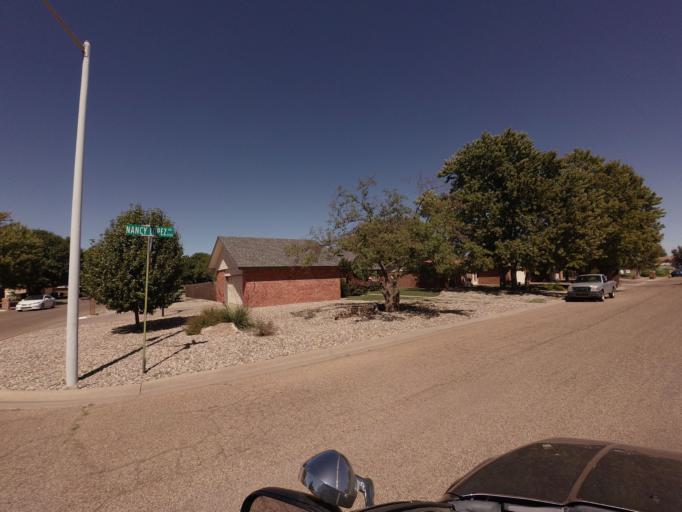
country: US
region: New Mexico
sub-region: Curry County
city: Clovis
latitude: 34.4422
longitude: -103.1807
